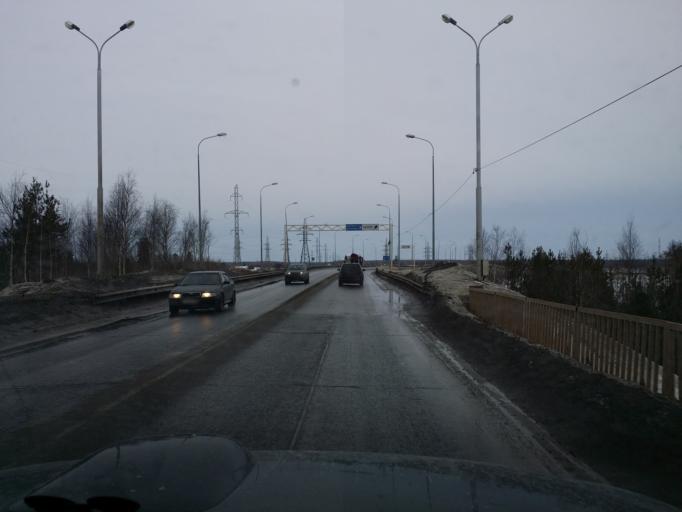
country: RU
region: Khanty-Mansiyskiy Avtonomnyy Okrug
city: Nizhnevartovsk
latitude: 60.9517
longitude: 76.6632
